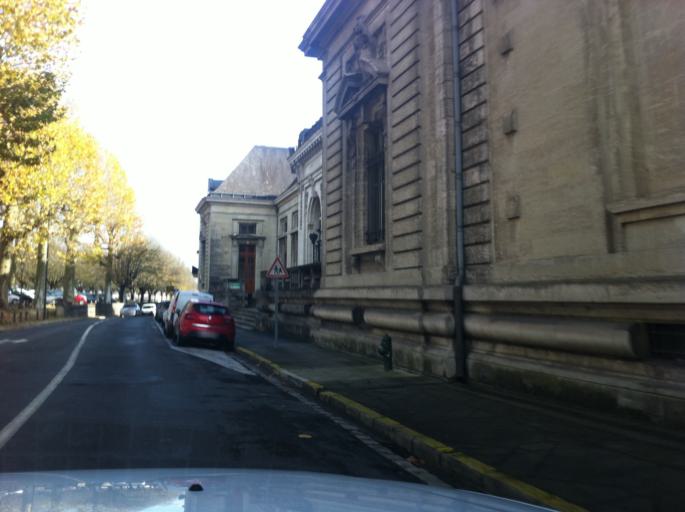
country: FR
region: Aquitaine
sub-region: Departement de la Dordogne
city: Perigueux
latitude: 45.1862
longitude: 0.7231
